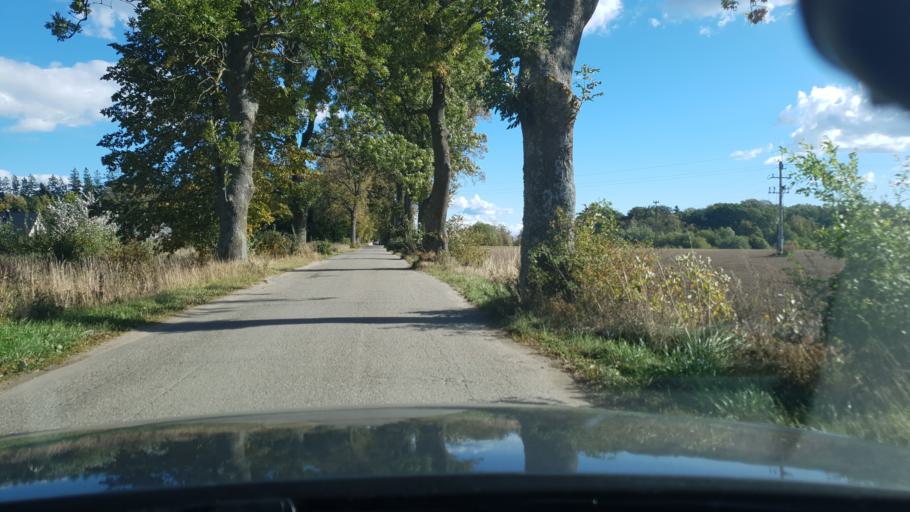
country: PL
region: Pomeranian Voivodeship
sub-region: Powiat pucki
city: Zelistrzewo
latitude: 54.6864
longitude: 18.4567
